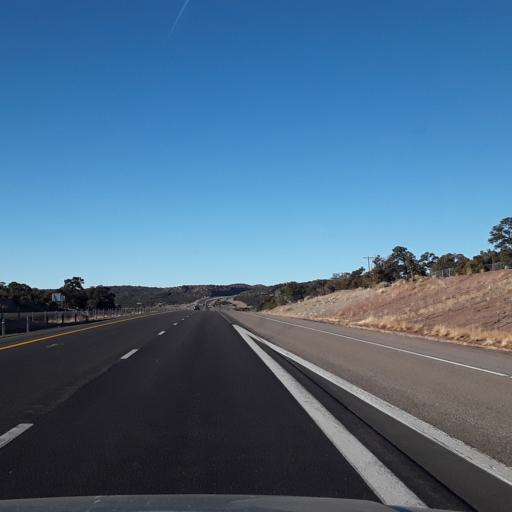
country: US
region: New Mexico
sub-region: Santa Fe County
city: Eldorado at Santa Fe
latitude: 35.5468
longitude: -105.8302
